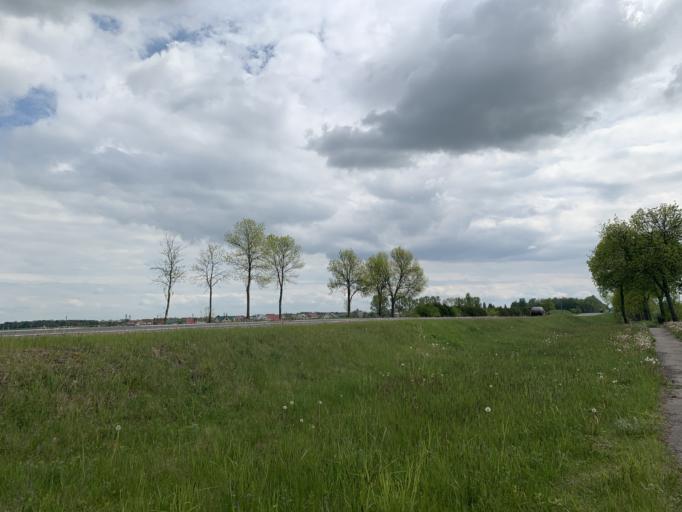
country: BY
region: Minsk
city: Nyasvizh
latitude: 53.2432
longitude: 26.6764
